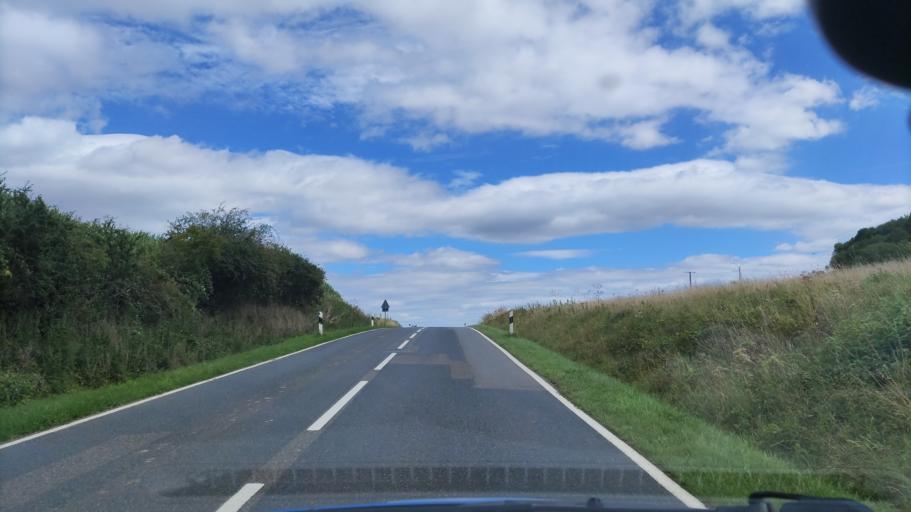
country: DE
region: Lower Saxony
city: Dassel
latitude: 51.8107
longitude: 9.6977
